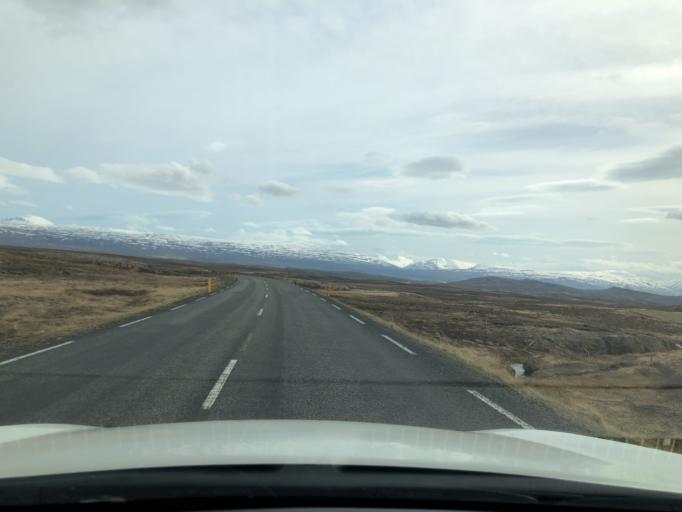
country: IS
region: East
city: Egilsstadir
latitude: 65.3616
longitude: -14.5242
